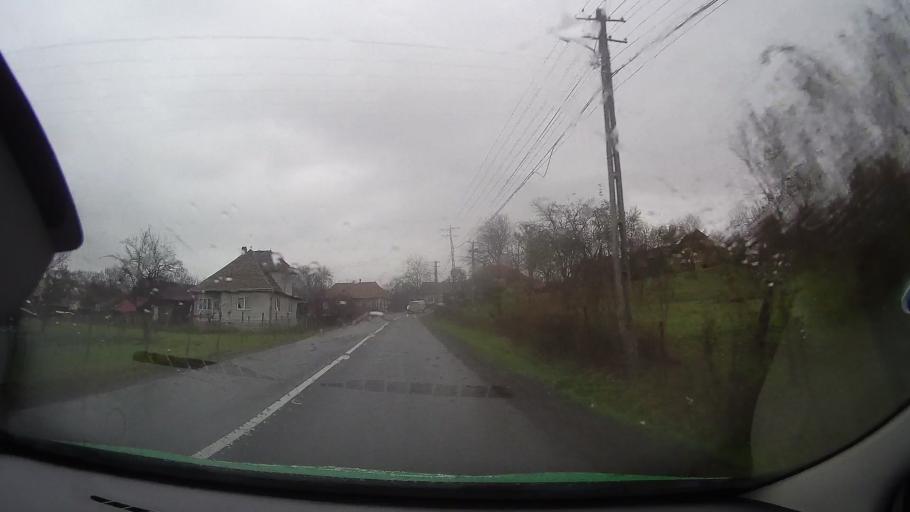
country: RO
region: Mures
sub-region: Comuna Vatava
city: Vatava
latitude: 46.9575
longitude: 24.7627
